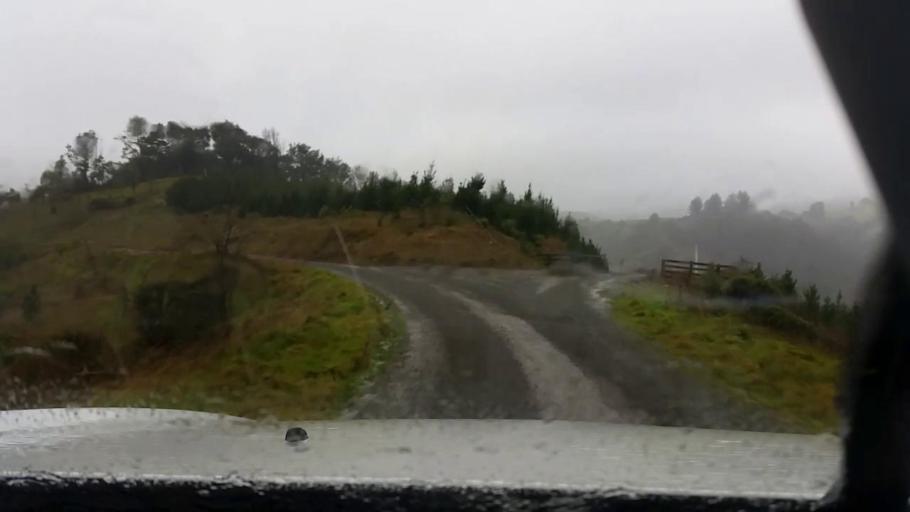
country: NZ
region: Wellington
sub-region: Masterton District
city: Masterton
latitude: -41.2002
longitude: 175.8107
